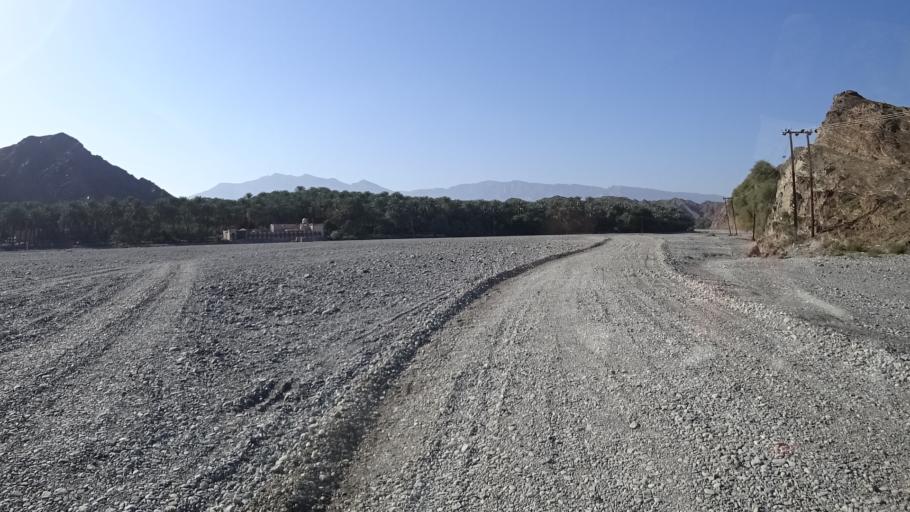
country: OM
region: Al Batinah
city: Bayt al `Awabi
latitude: 23.3922
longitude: 57.6624
